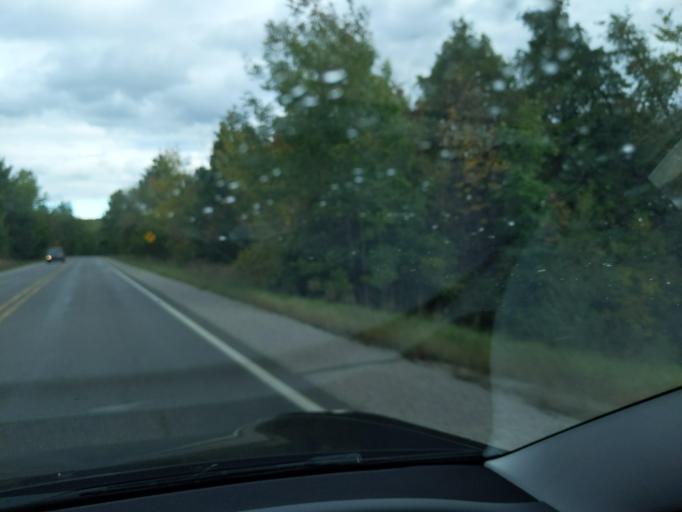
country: US
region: Michigan
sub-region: Kalkaska County
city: Rapid City
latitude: 44.8041
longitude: -85.2764
